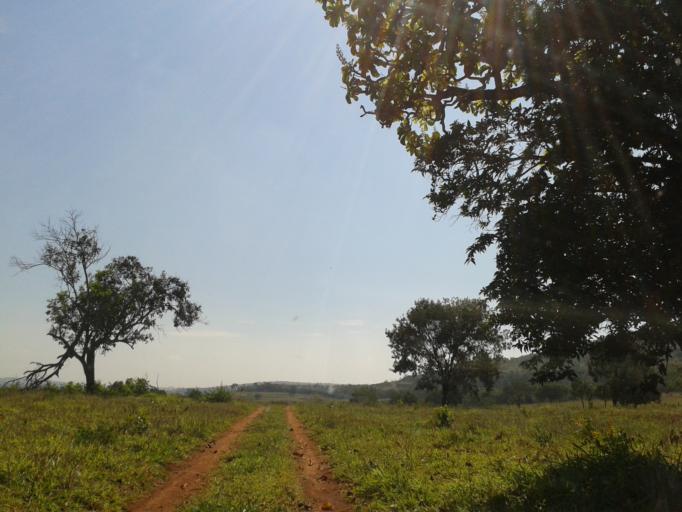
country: BR
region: Minas Gerais
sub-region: Campina Verde
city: Campina Verde
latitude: -19.3885
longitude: -49.6321
